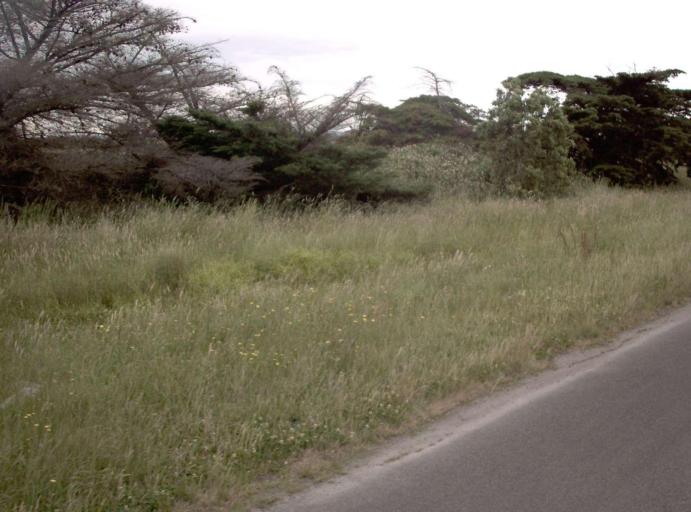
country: AU
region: Victoria
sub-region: Cardinia
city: Koo-Wee-Rup
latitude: -38.2249
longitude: 145.5097
